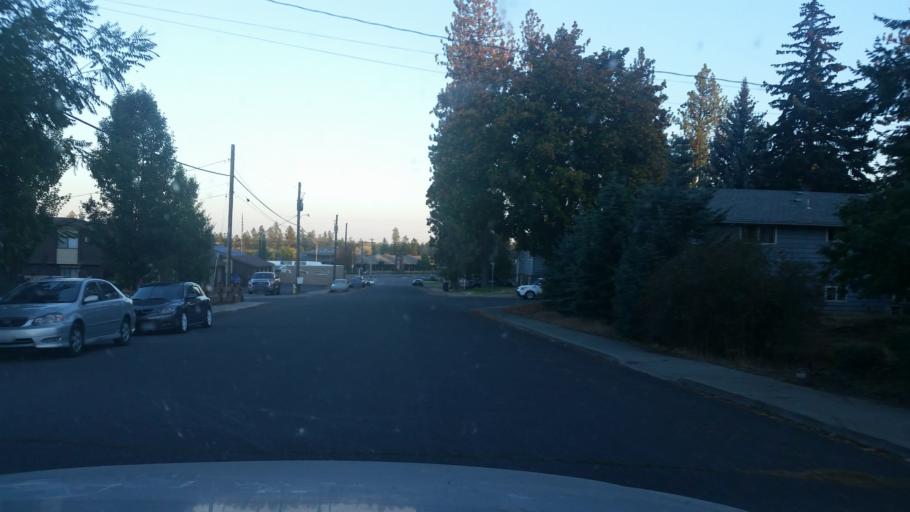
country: US
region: Washington
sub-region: Spokane County
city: Cheney
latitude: 47.4996
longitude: -117.5674
